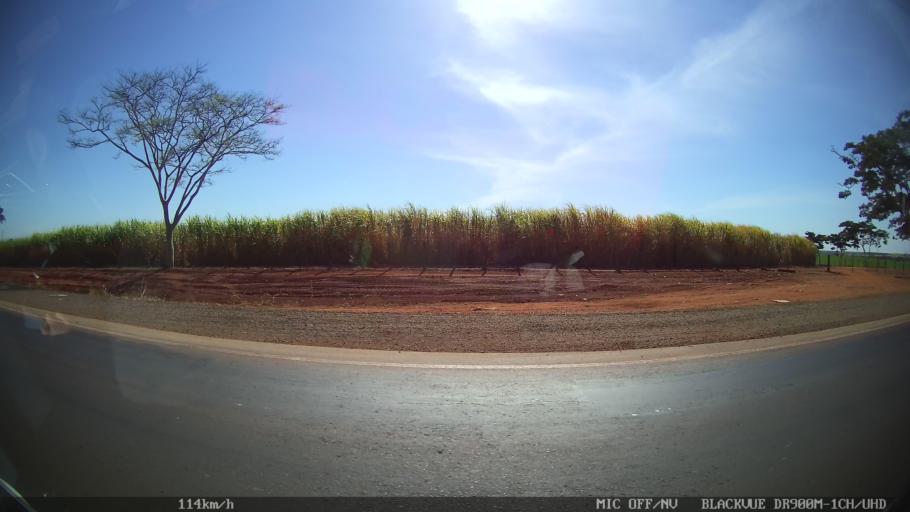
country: BR
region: Sao Paulo
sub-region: Olimpia
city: Olimpia
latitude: -20.6368
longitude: -48.8210
